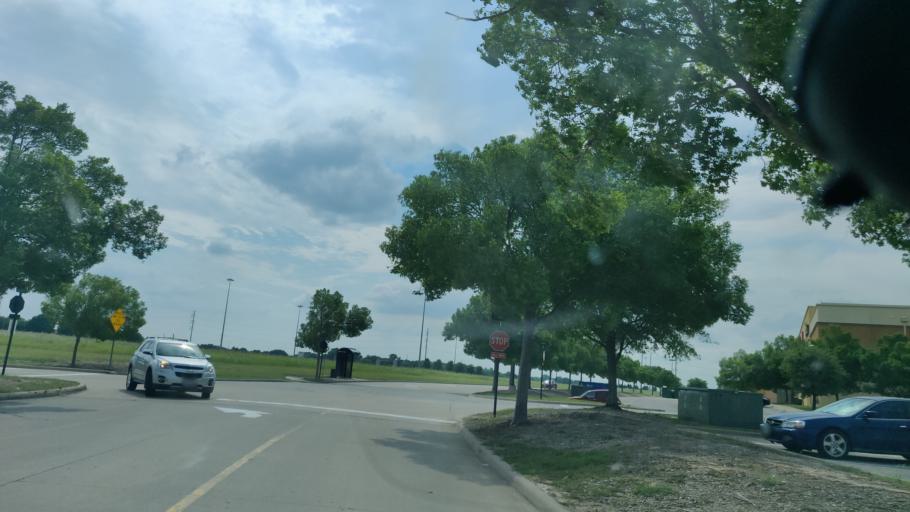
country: US
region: Texas
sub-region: Dallas County
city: Sachse
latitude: 32.9495
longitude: -96.6129
